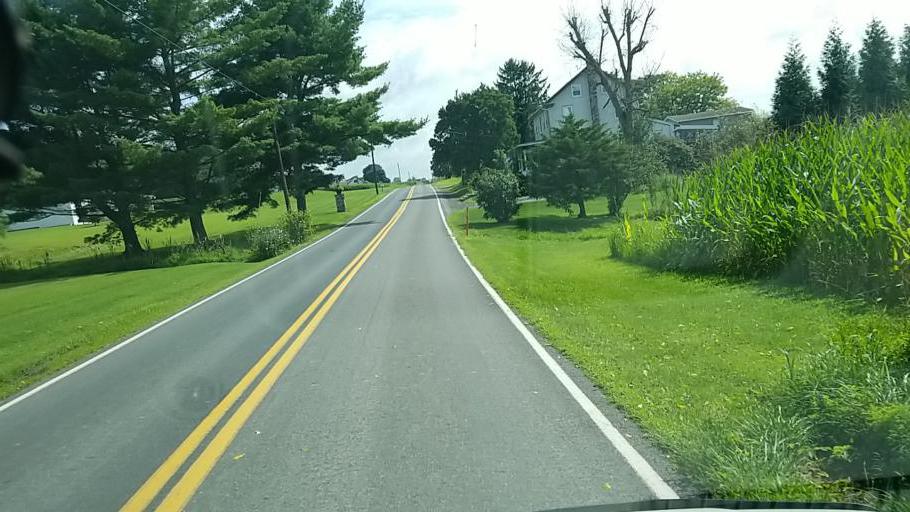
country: US
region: Pennsylvania
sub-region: Dauphin County
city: Millersburg
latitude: 40.5868
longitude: -76.9134
